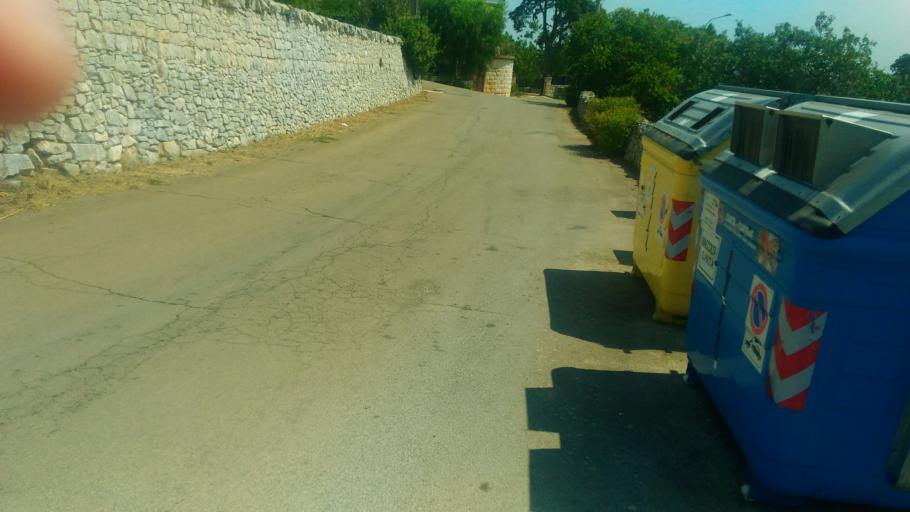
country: IT
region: Apulia
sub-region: Provincia di Brindisi
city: Cisternino
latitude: 40.7467
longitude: 17.3760
